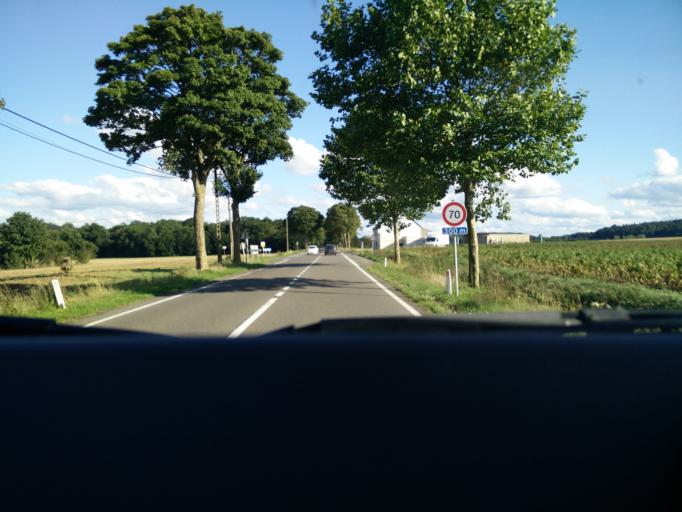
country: BE
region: Wallonia
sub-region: Province du Hainaut
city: Merbes-le-Chateau
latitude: 50.2909
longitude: 4.1725
